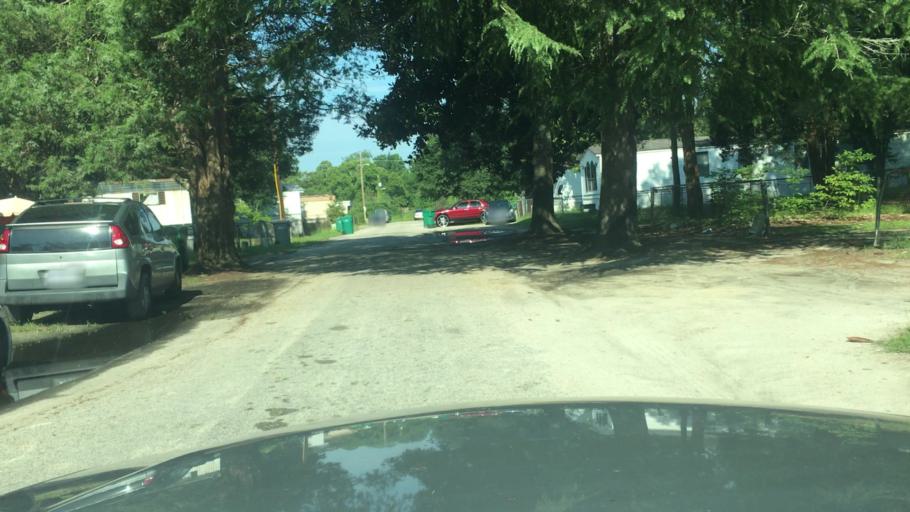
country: US
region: North Carolina
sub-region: Cumberland County
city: Spring Lake
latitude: 35.1519
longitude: -78.9154
